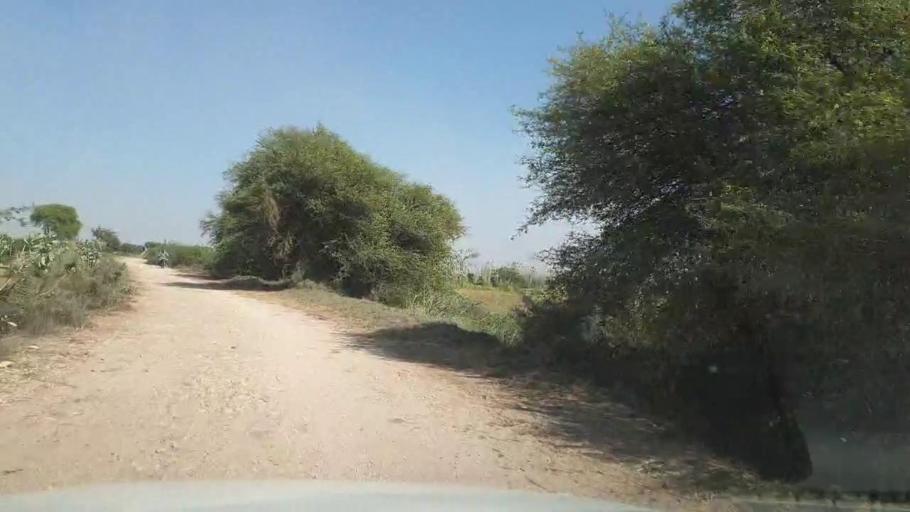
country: PK
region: Sindh
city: Mirpur Sakro
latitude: 24.4103
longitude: 67.7596
